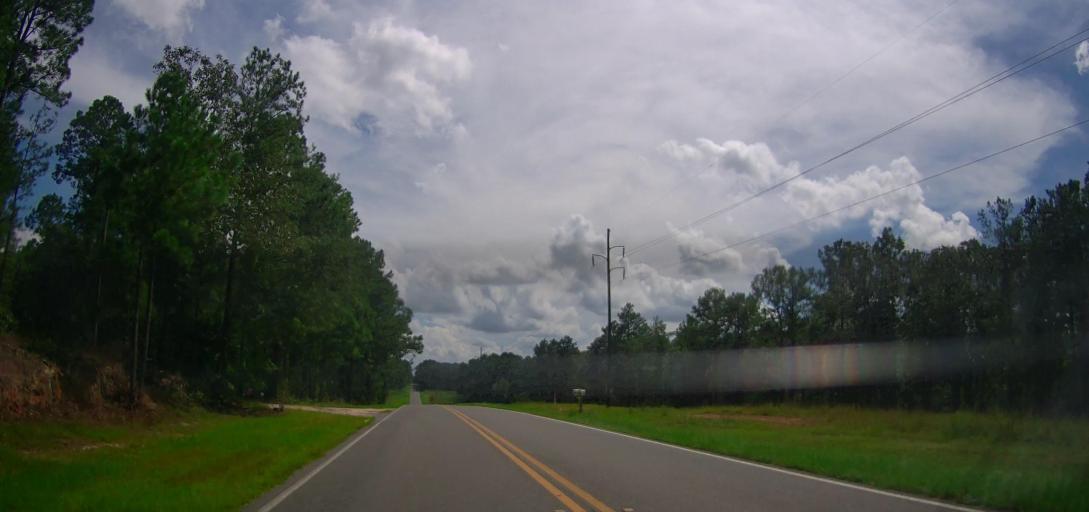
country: US
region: Georgia
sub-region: Taylor County
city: Butler
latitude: 32.5144
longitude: -84.2048
